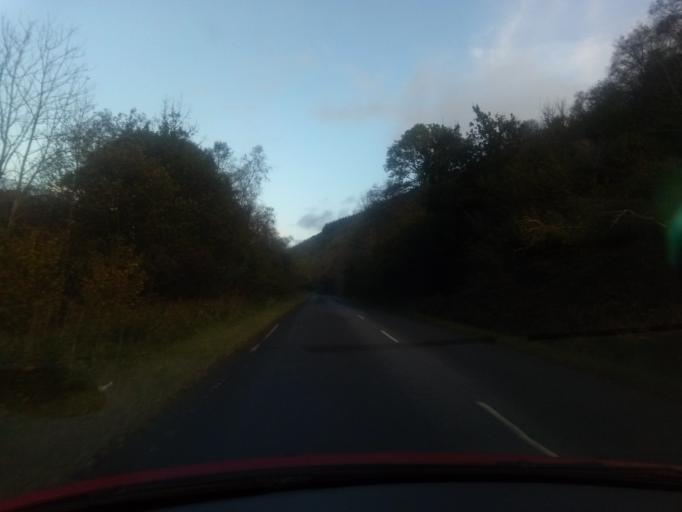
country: GB
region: Scotland
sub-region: The Scottish Borders
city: Hawick
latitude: 55.3549
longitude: -2.6481
